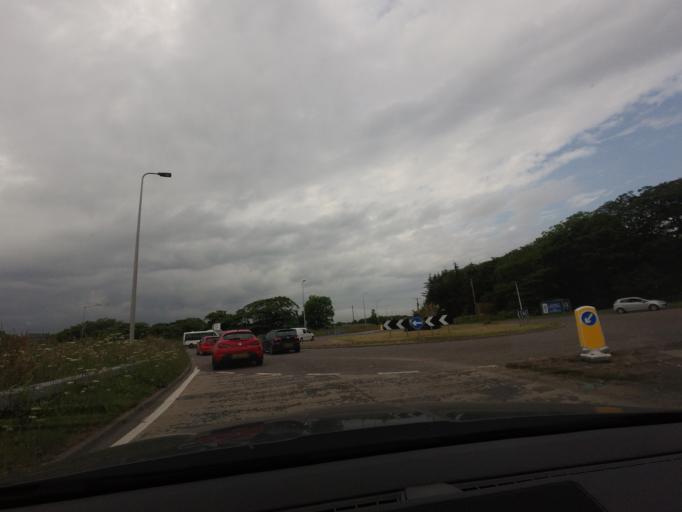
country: GB
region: Scotland
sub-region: Aberdeenshire
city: Peterhead
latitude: 57.5071
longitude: -1.8262
